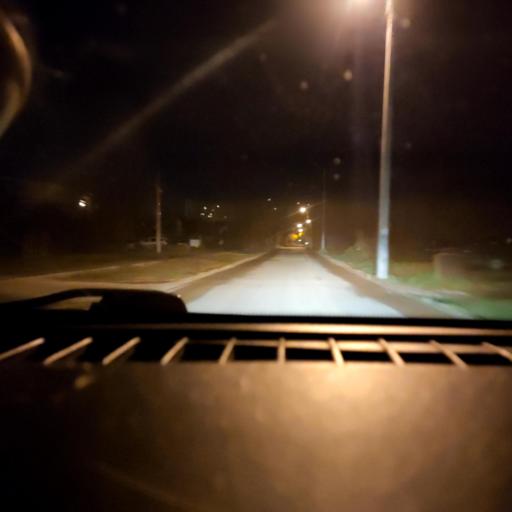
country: RU
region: Perm
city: Perm
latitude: 57.9797
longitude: 56.2977
